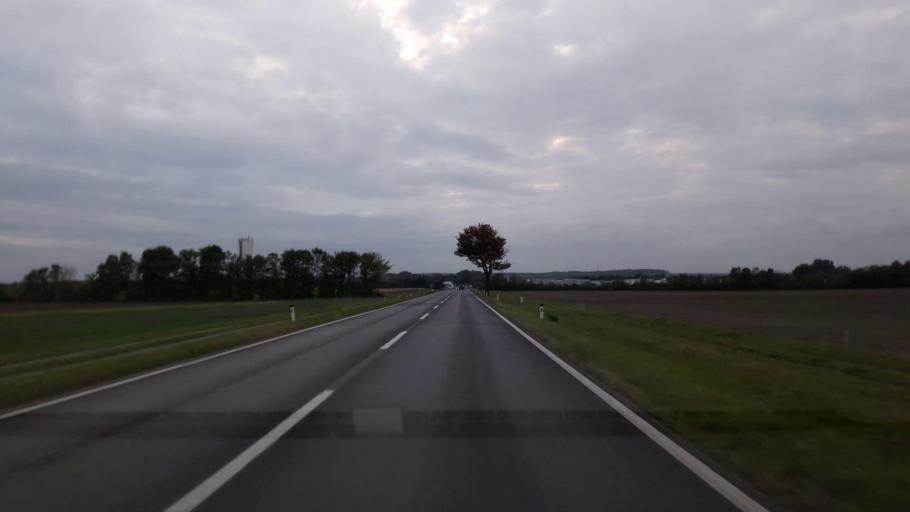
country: AT
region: Lower Austria
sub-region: Politischer Bezirk Bruck an der Leitha
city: Enzersdorf an der Fischa
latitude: 48.0673
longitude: 16.6007
